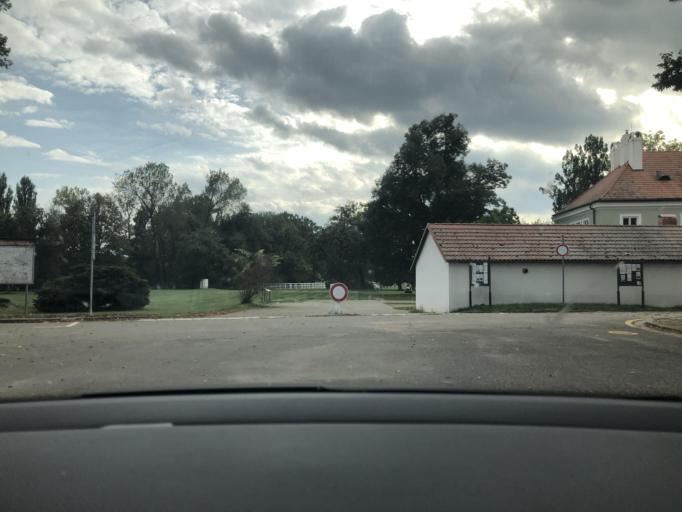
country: CZ
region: Pardubicky
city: Recany nad Labem
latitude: 50.0572
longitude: 15.4867
